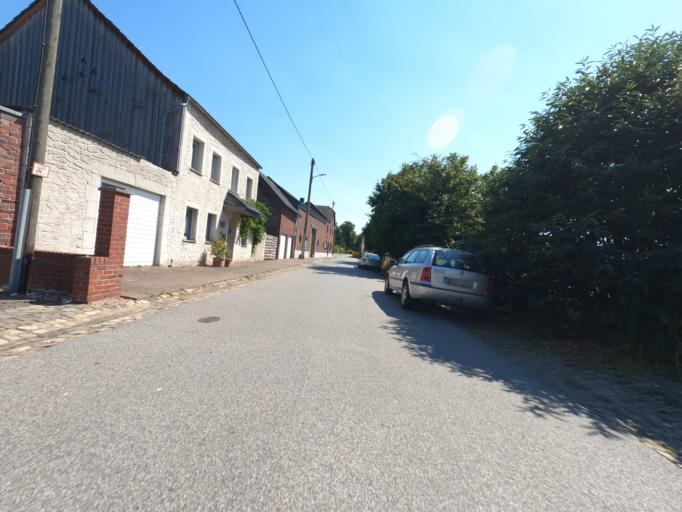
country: DE
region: North Rhine-Westphalia
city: Erkelenz
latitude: 51.0918
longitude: 6.3017
